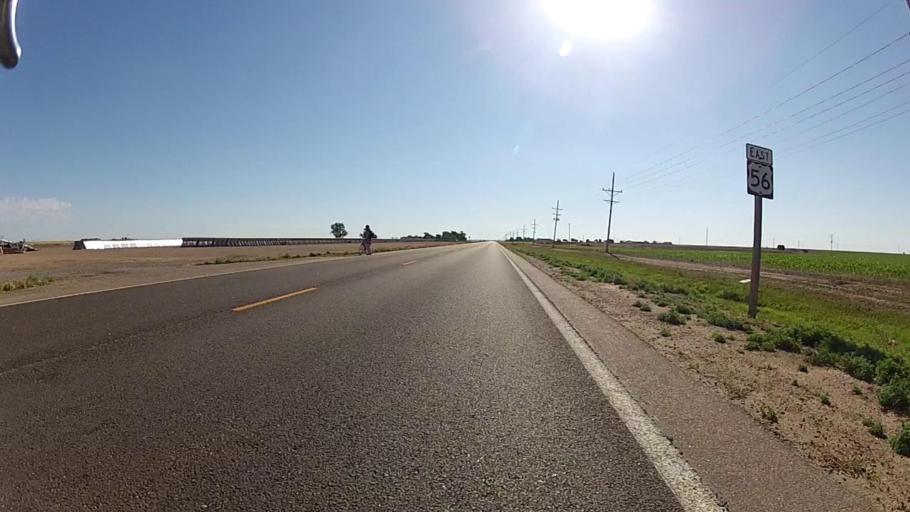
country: US
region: Kansas
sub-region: Haskell County
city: Sublette
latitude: 37.5444
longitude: -100.6236
